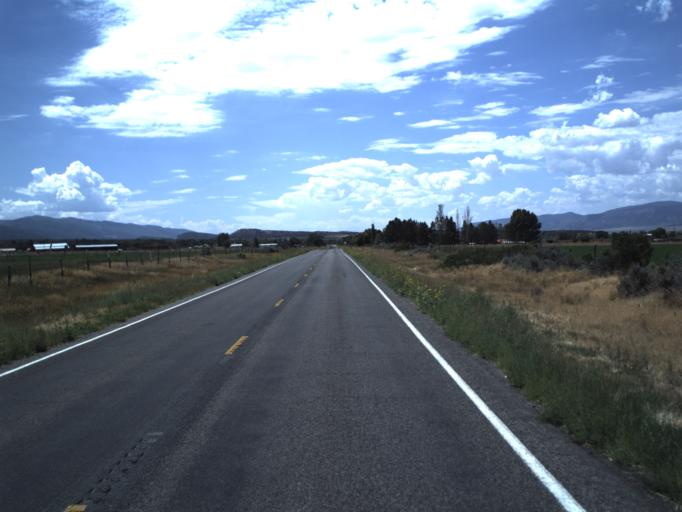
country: US
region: Utah
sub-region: Sanpete County
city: Mount Pleasant
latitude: 39.5056
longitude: -111.4849
